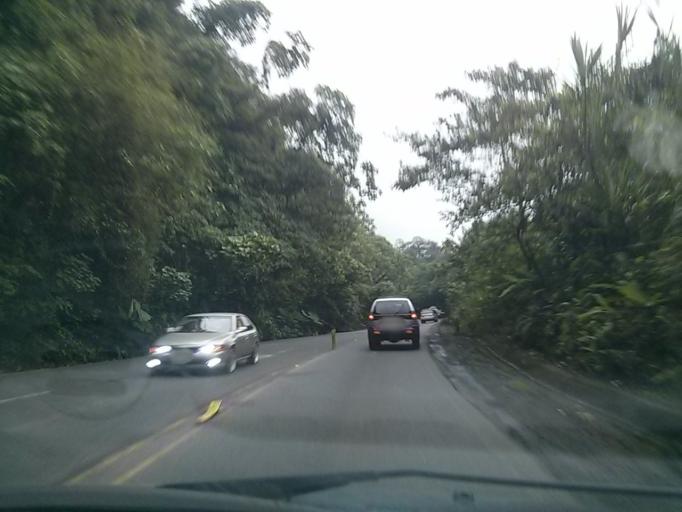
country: CR
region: San Jose
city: Dulce Nombre de Jesus
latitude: 10.0892
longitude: -83.9820
